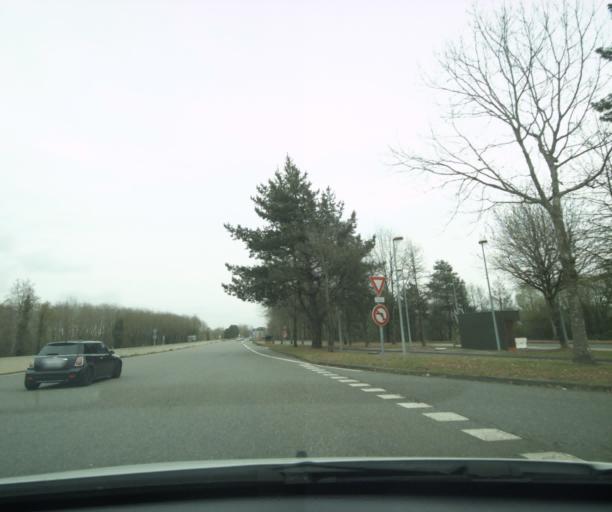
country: FR
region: Aquitaine
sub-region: Departement des Pyrenees-Atlantiques
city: Bardos
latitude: 43.5299
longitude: -1.1852
